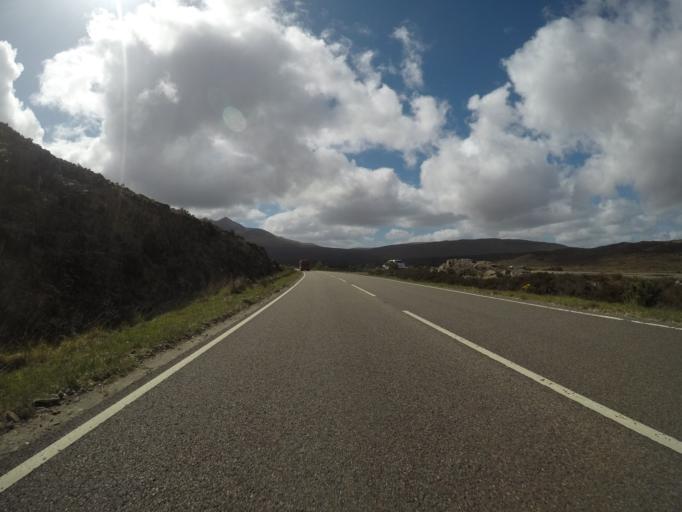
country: GB
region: Scotland
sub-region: Highland
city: Isle of Skye
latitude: 57.2930
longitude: -6.1672
